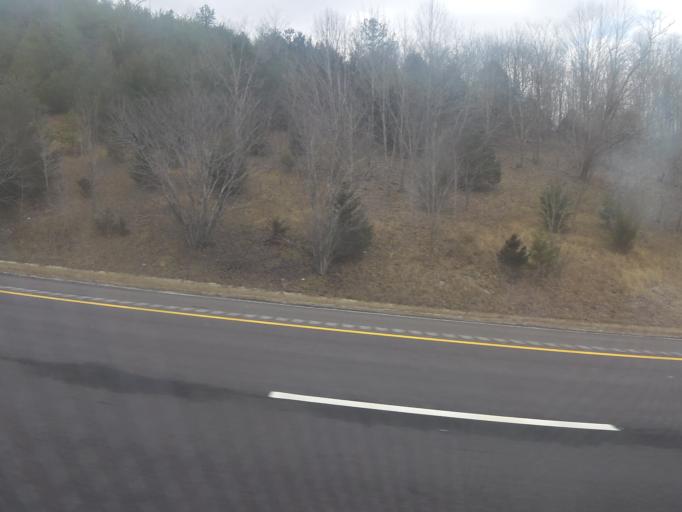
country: US
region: Tennessee
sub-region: Marion County
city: Monteagle
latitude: 35.1879
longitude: -85.8150
